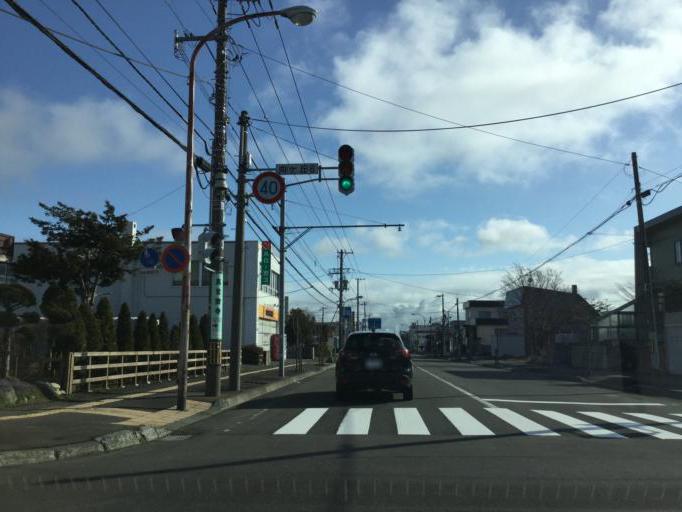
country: JP
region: Hokkaido
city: Ebetsu
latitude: 43.1058
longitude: 141.5352
